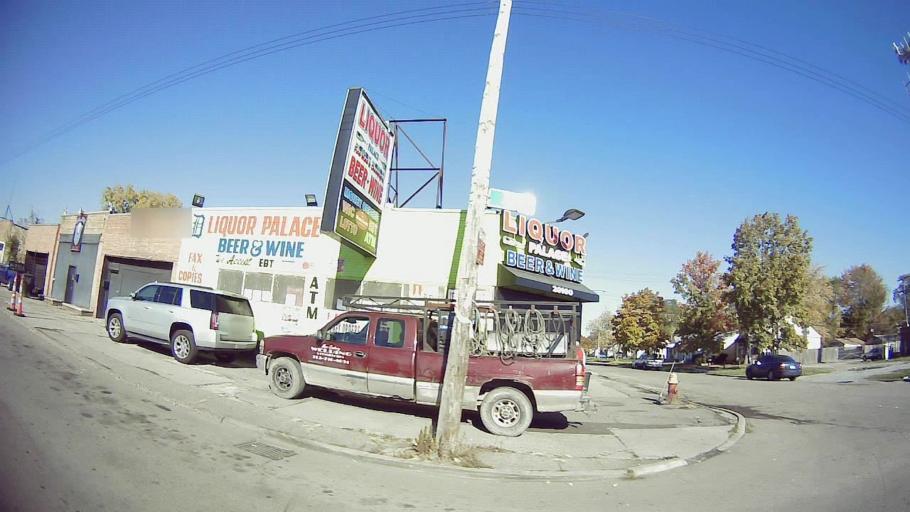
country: US
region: Michigan
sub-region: Wayne County
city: Dearborn Heights
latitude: 42.3576
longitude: -83.2373
